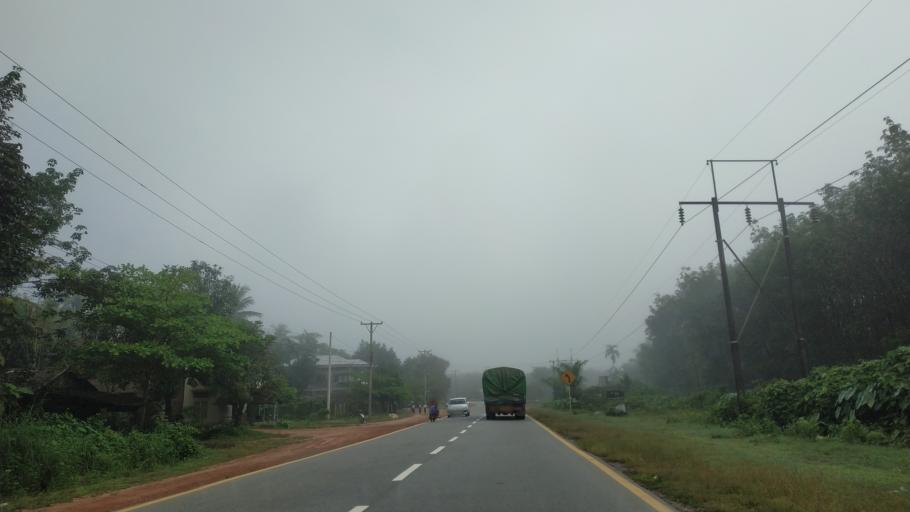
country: MM
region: Tanintharyi
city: Dawei
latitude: 14.1805
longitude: 98.2090
